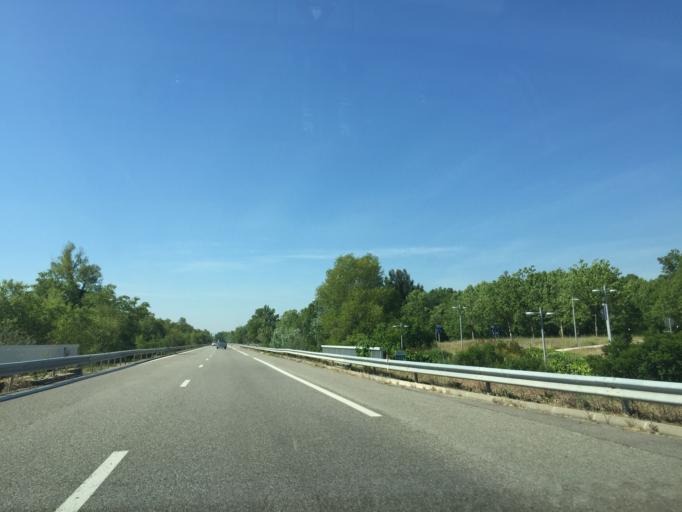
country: FR
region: Provence-Alpes-Cote d'Azur
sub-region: Departement des Alpes-de-Haute-Provence
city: Volx
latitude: 43.8432
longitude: 5.8493
